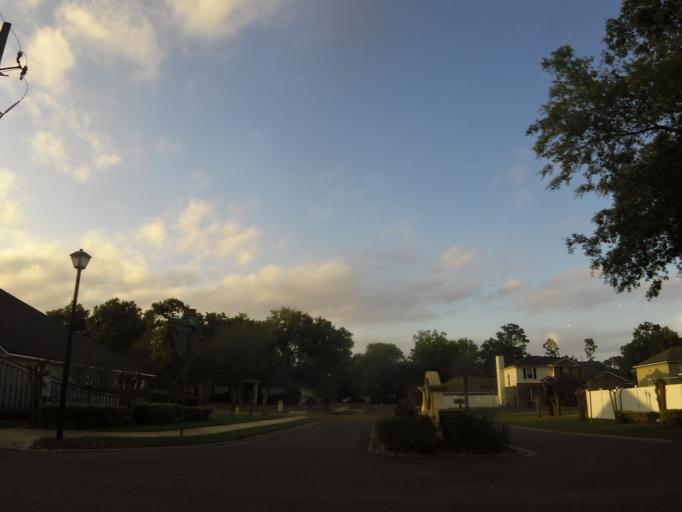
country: US
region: Florida
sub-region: Duval County
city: Jacksonville
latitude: 30.4398
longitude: -81.6211
